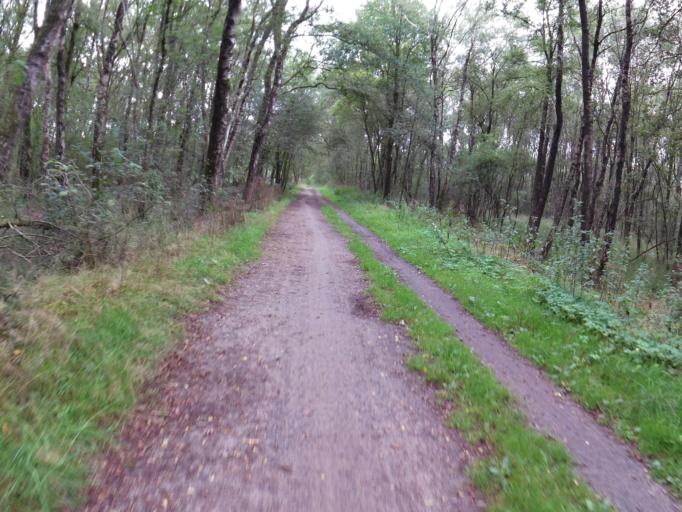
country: NL
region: Gelderland
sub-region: Berkelland
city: Eibergen
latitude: 52.0435
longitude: 6.6896
